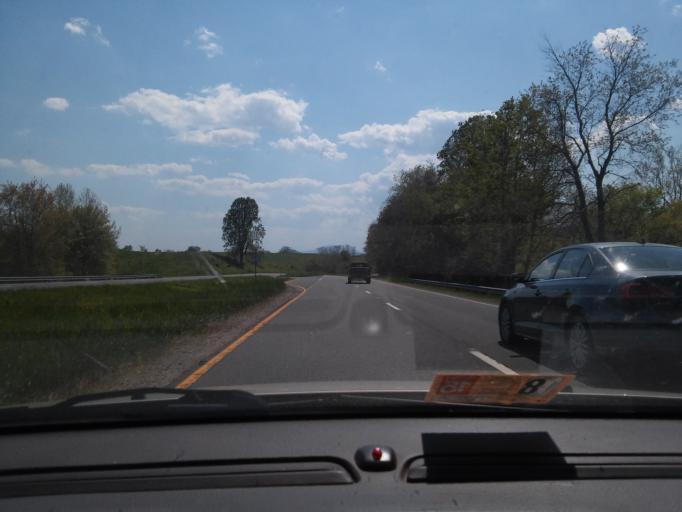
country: US
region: Virginia
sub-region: Rappahannock County
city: Washington
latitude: 38.7173
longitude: -78.1247
